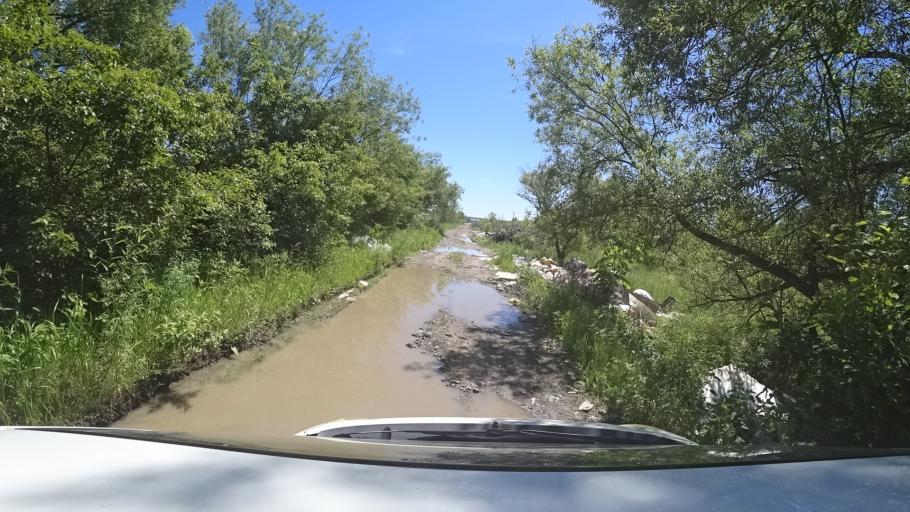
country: RU
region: Khabarovsk Krai
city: Topolevo
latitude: 48.4867
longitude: 135.1767
